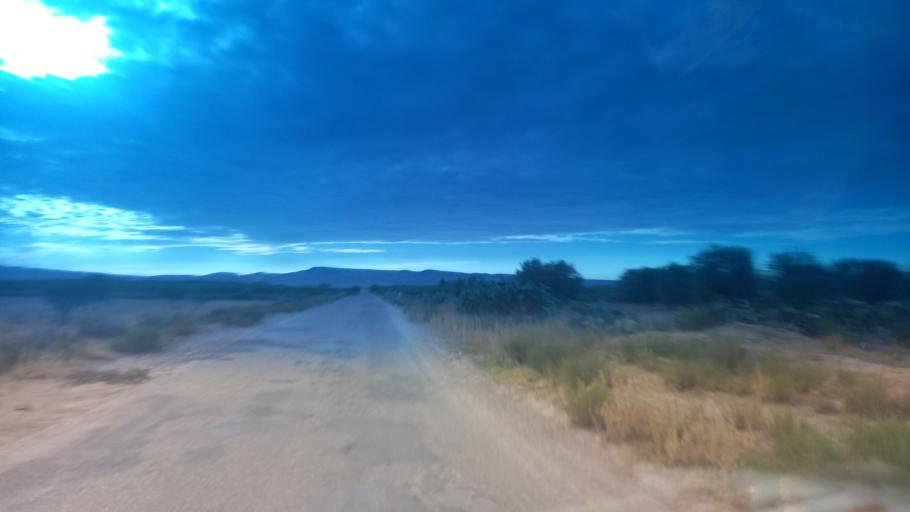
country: TN
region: Al Qasrayn
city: Sbiba
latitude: 35.3856
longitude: 9.0333
